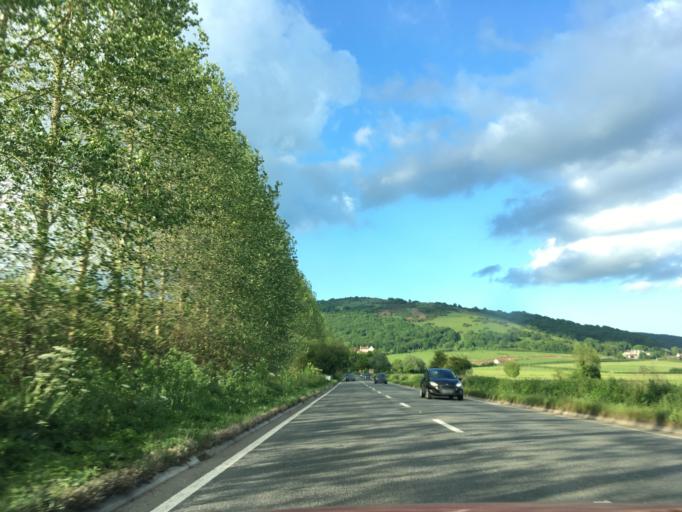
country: GB
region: England
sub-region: Somerset
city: Axbridge
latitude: 51.2858
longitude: -2.8399
